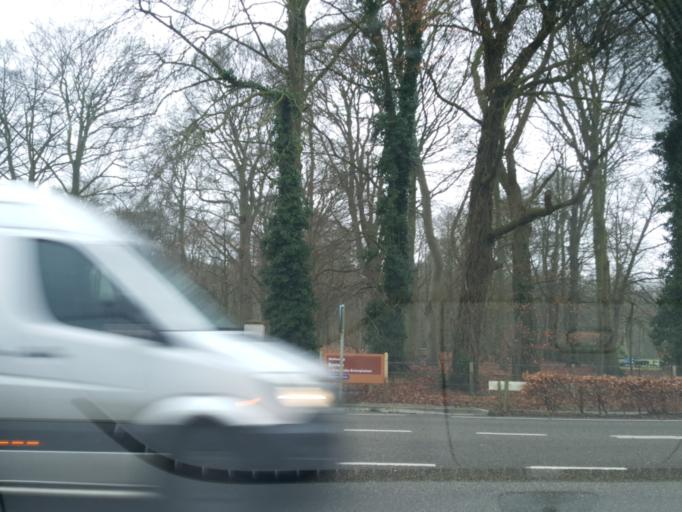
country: NL
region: North Holland
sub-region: Gemeente Bussum
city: Bussum
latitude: 52.2599
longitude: 5.1394
